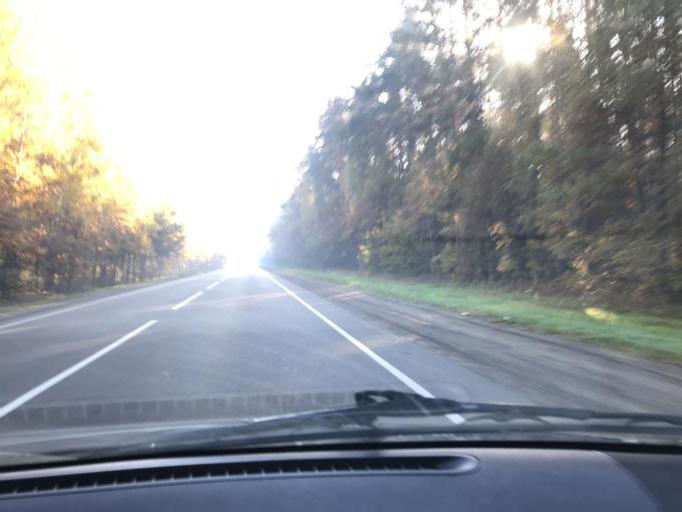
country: BY
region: Brest
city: Horad Luninyets
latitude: 52.2875
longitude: 26.7903
